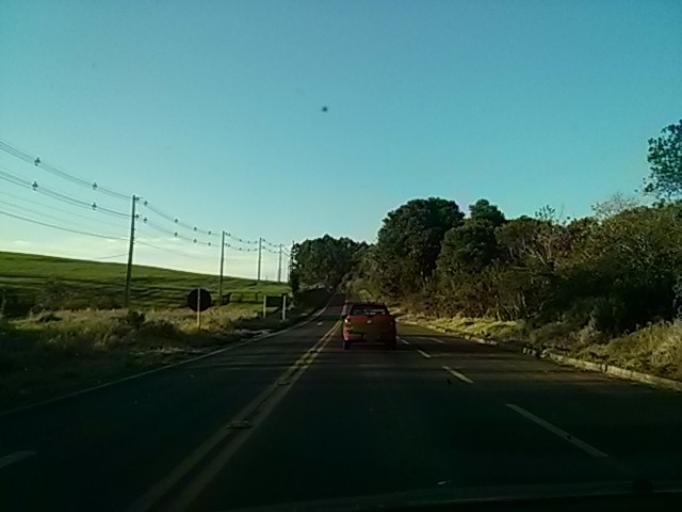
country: BR
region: Santa Catarina
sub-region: Chapeco
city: Chapeco
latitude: -27.1086
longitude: -52.7095
